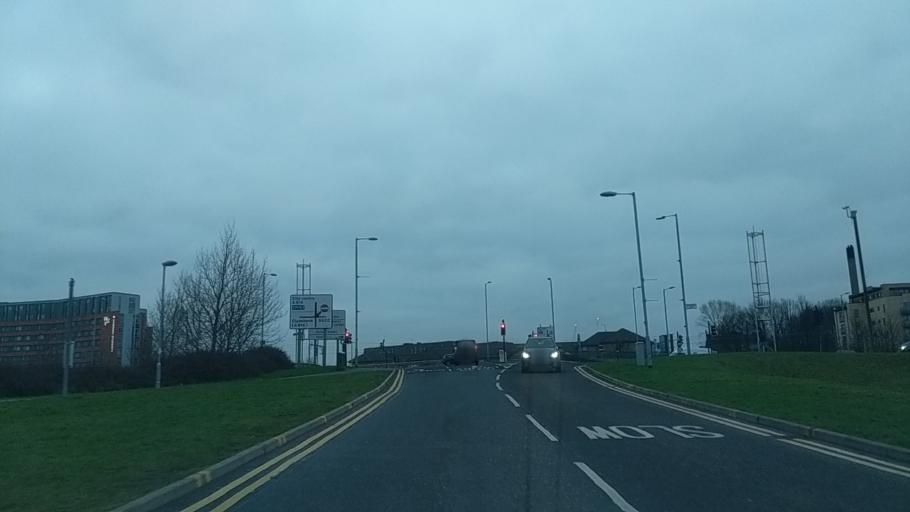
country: GB
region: Scotland
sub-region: Glasgow City
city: Glasgow
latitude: 55.8663
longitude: -4.3048
